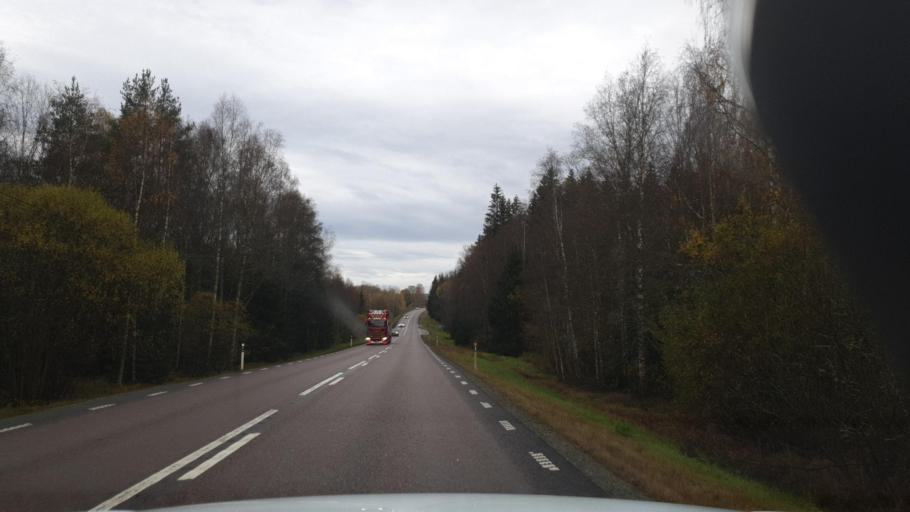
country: SE
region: Vaermland
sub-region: Sunne Kommun
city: Sunne
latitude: 59.6665
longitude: 12.9005
